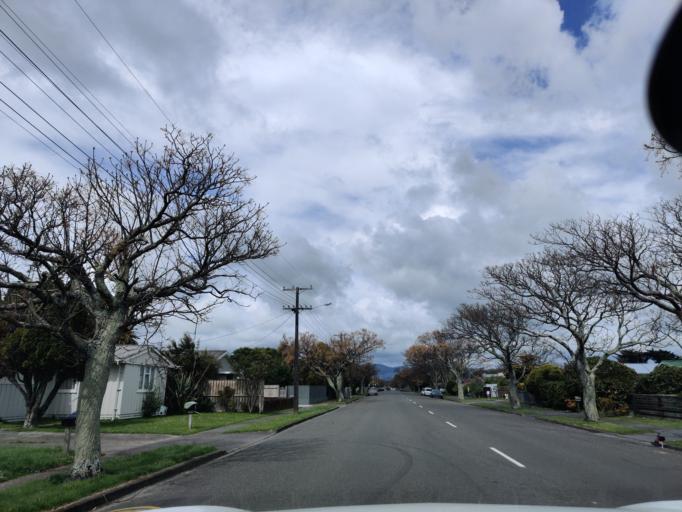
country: NZ
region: Manawatu-Wanganui
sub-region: Palmerston North City
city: Palmerston North
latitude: -40.3732
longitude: 175.5800
